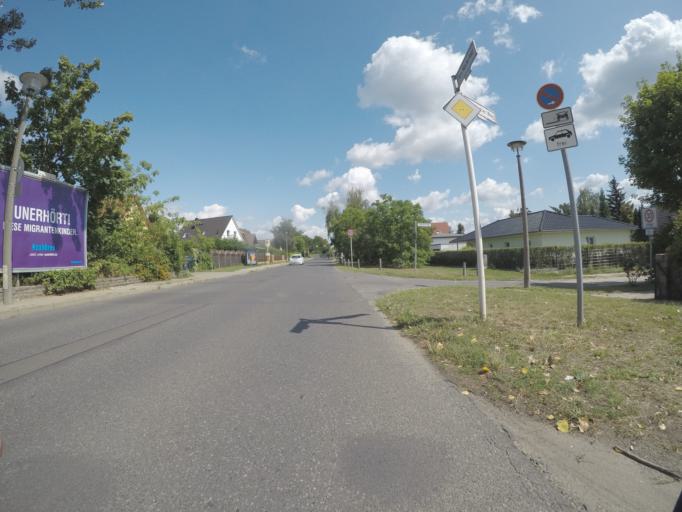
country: DE
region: Berlin
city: Kaulsdorf
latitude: 52.5028
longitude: 13.5852
